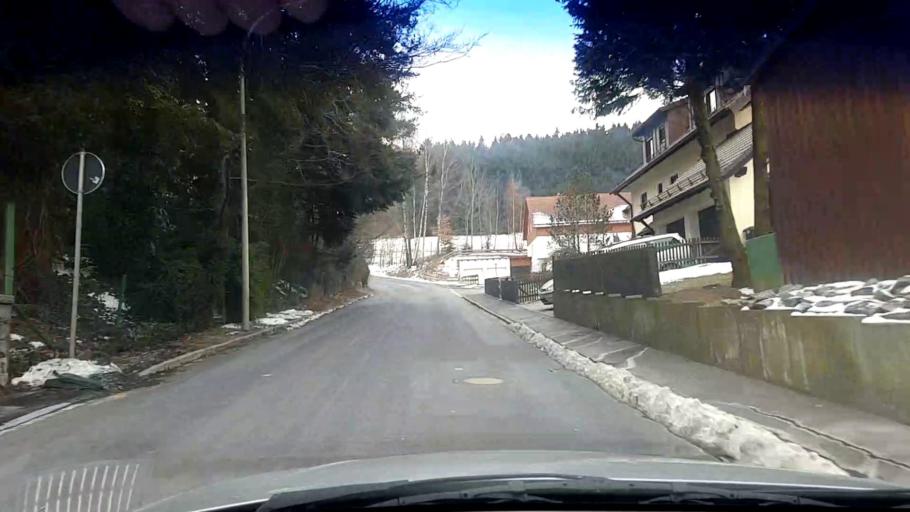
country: DE
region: Bavaria
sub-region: Upper Franconia
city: Gefrees
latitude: 50.0912
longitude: 11.7435
